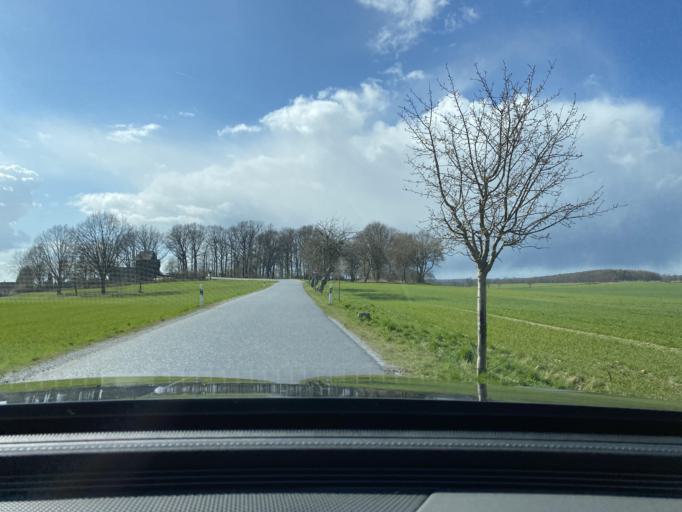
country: DE
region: Saxony
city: Radibor
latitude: 51.2487
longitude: 14.3632
